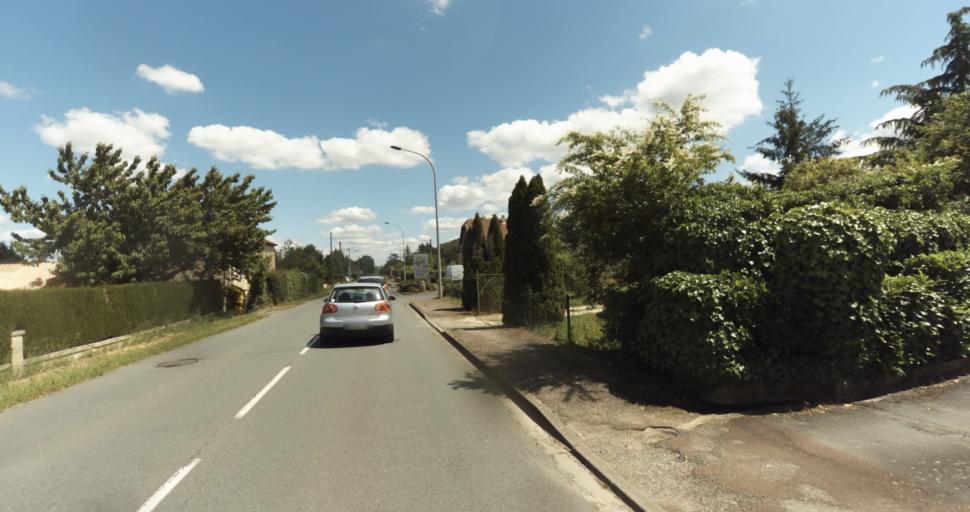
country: FR
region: Aquitaine
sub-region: Departement de la Dordogne
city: Le Bugue
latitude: 44.8456
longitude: 0.9174
